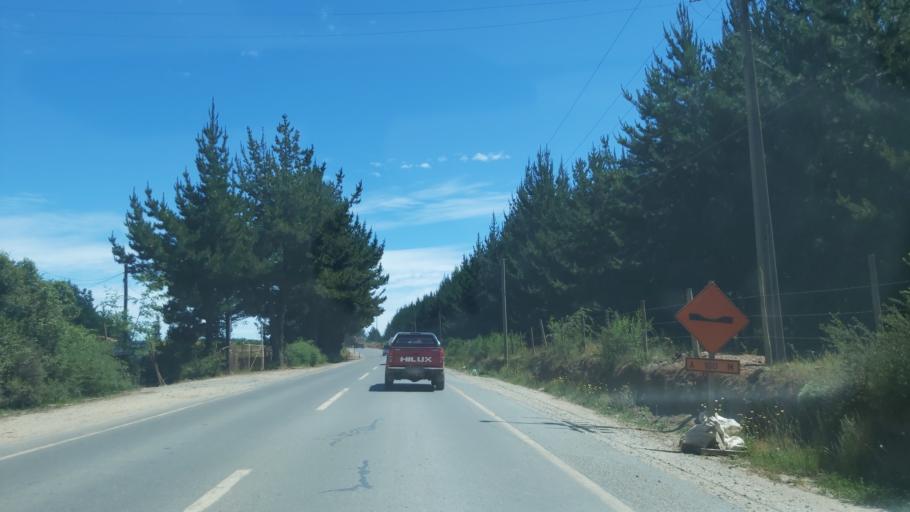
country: CL
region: Maule
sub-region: Provincia de Talca
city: Constitucion
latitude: -35.3939
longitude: -72.4278
